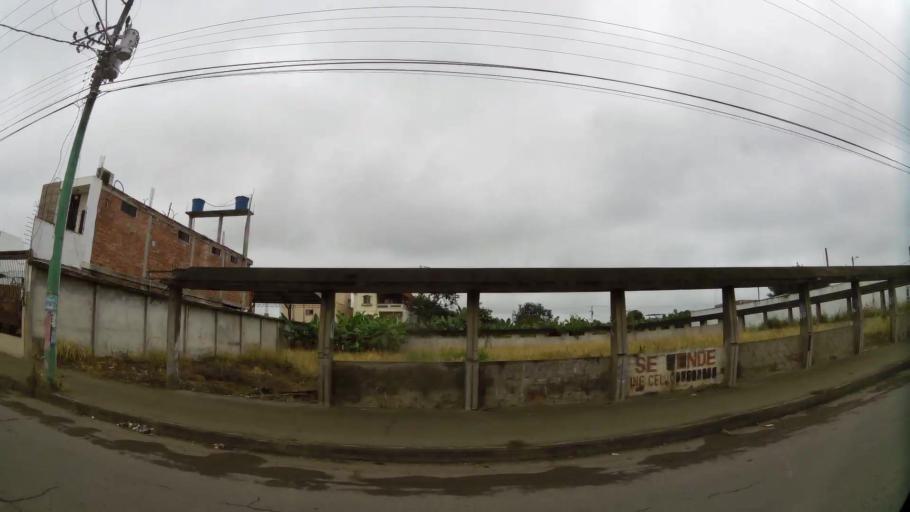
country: EC
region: El Oro
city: Pasaje
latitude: -3.3270
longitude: -79.8223
